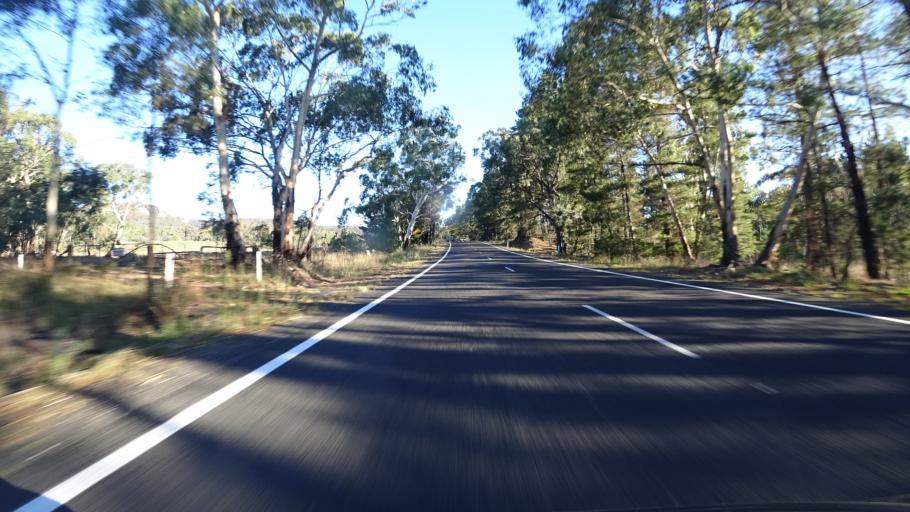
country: AU
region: New South Wales
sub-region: Lithgow
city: Portland
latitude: -33.3163
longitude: 150.0369
